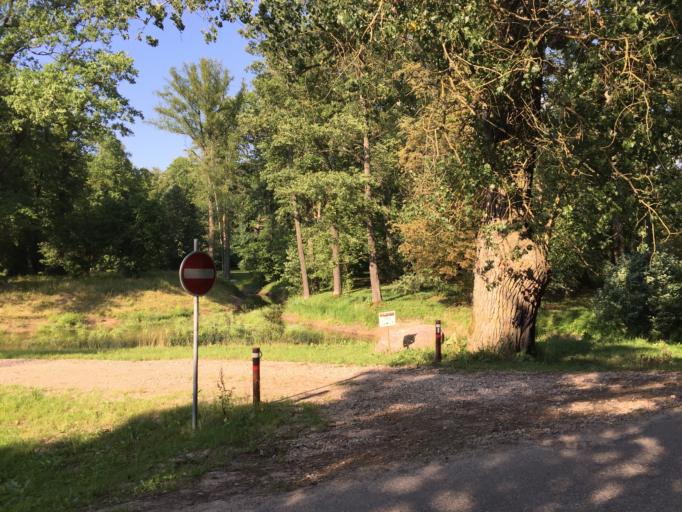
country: LT
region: Siauliu apskritis
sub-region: Joniskis
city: Joniskis
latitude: 56.4231
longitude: 23.6965
